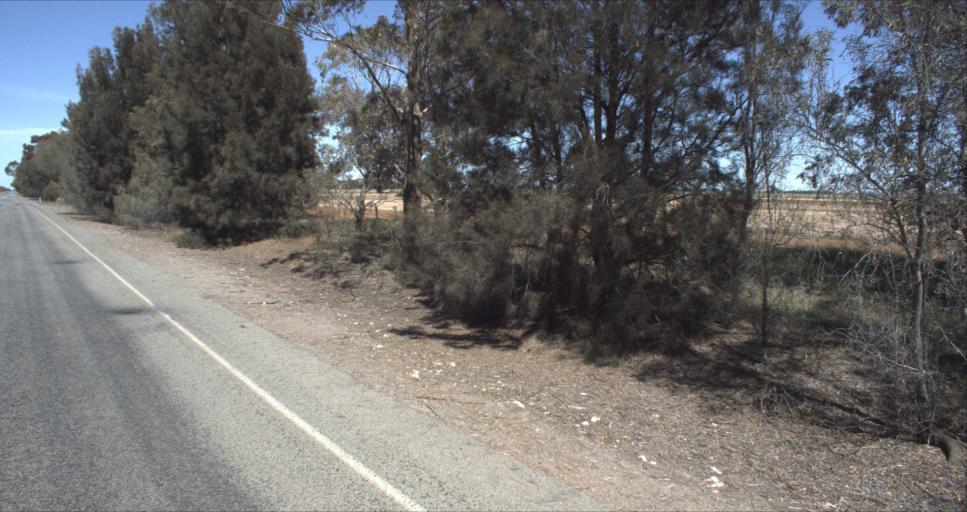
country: AU
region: New South Wales
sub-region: Leeton
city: Leeton
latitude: -34.4670
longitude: 146.2931
